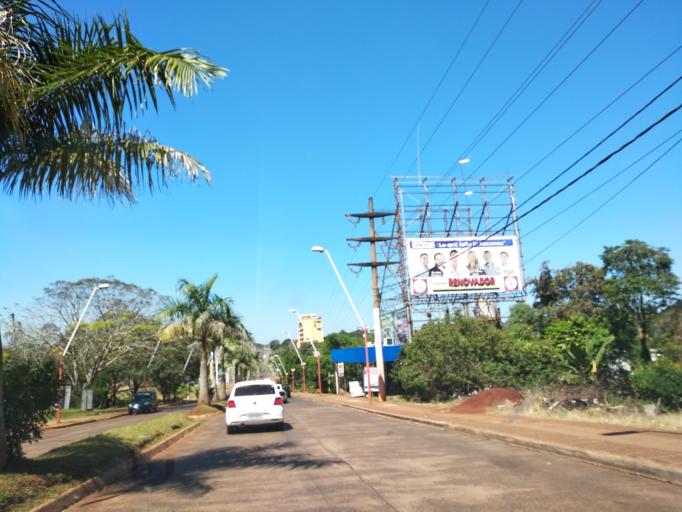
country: AR
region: Misiones
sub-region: Departamento de Iguazu
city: Puerto Iguazu
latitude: -25.6084
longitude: -54.5657
